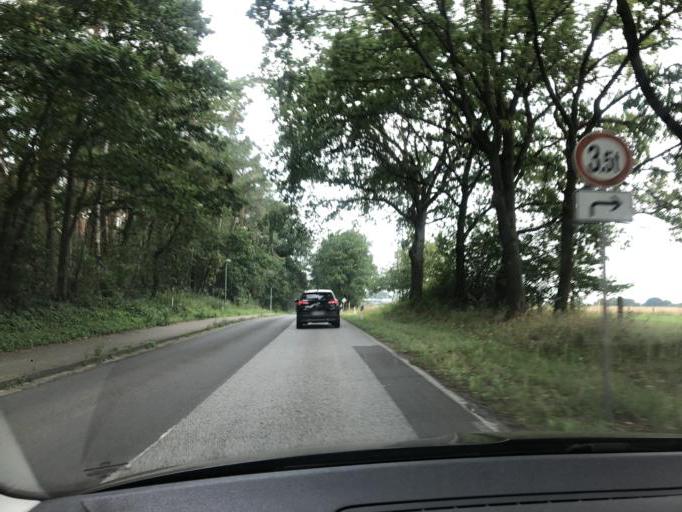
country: DE
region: Mecklenburg-Vorpommern
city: Stralendorf
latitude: 53.5713
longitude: 11.3292
